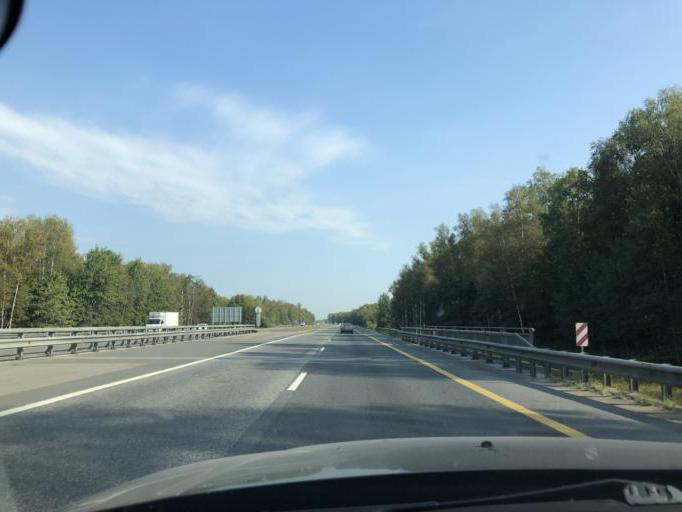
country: RU
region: Moskovskaya
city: Danki
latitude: 54.9243
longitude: 37.5194
